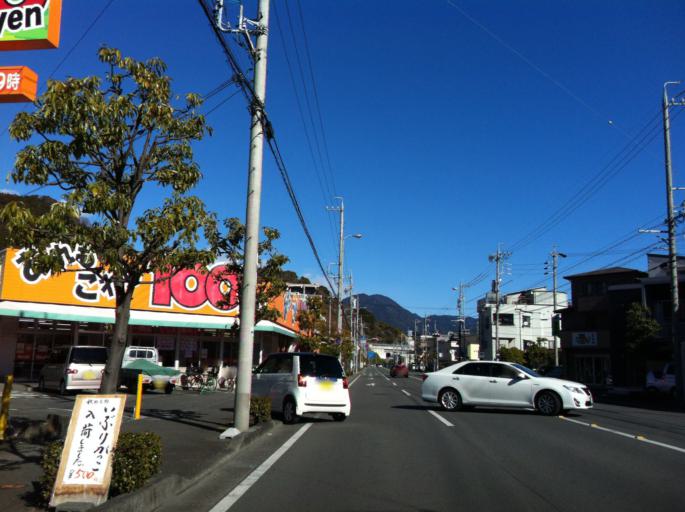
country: JP
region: Shizuoka
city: Shizuoka-shi
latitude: 34.9991
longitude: 138.3801
